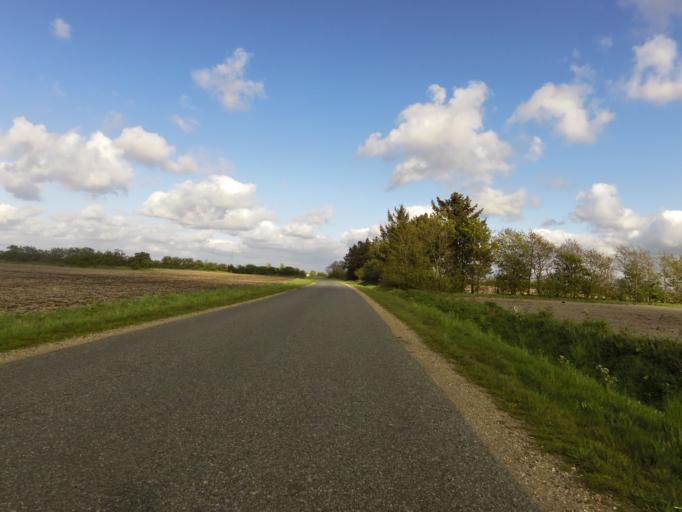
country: DK
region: South Denmark
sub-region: Esbjerg Kommune
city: Ribe
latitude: 55.2585
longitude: 8.7954
